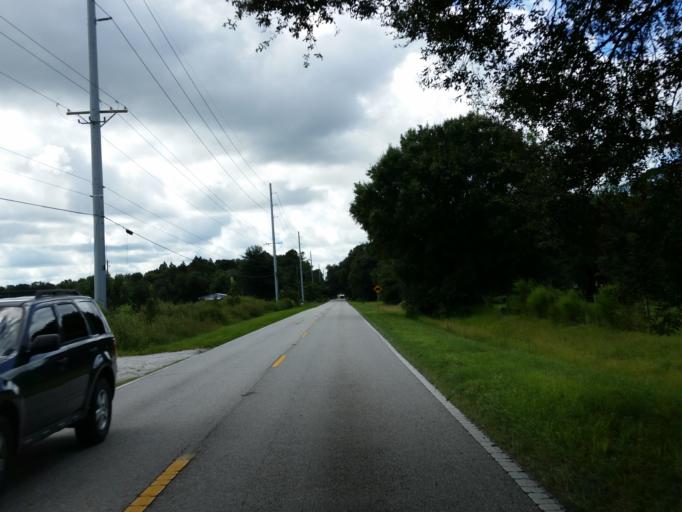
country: US
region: Florida
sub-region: Hillsborough County
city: Pebble Creek
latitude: 28.1676
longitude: -82.2634
